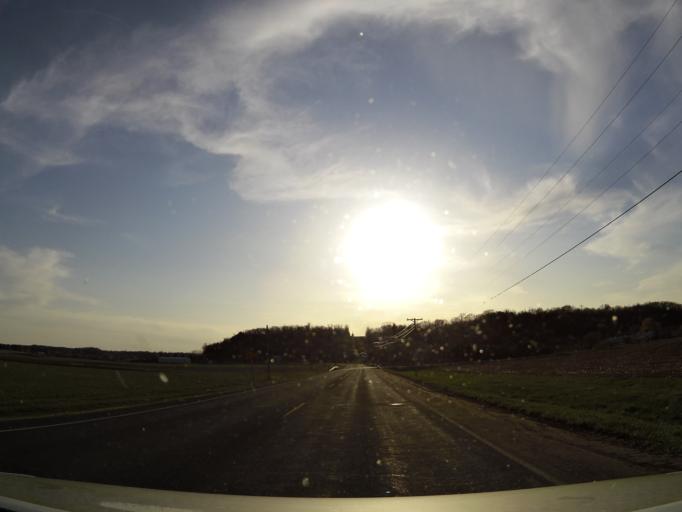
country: US
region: Wisconsin
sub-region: Pierce County
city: River Falls
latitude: 44.8771
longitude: -92.6579
